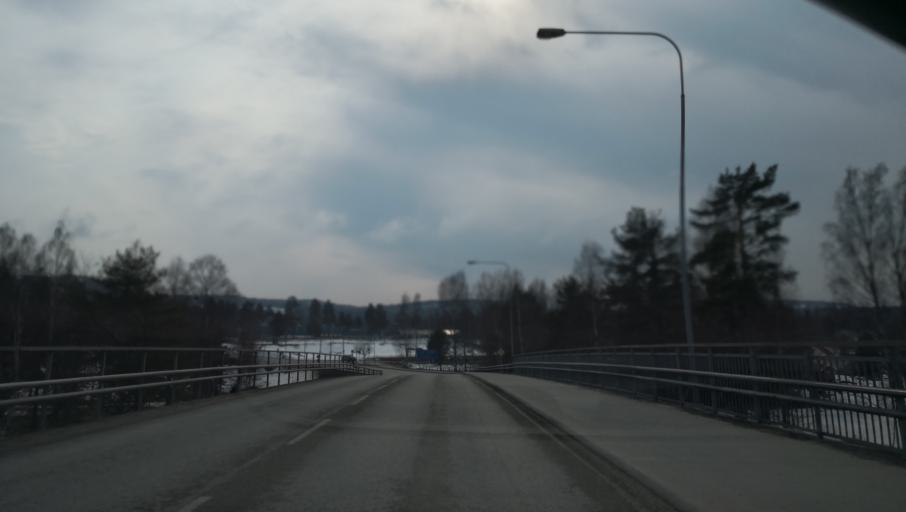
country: SE
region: Vaesternorrland
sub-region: OErnskoeldsviks Kommun
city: Ornskoldsvik
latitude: 63.2912
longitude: 18.6106
